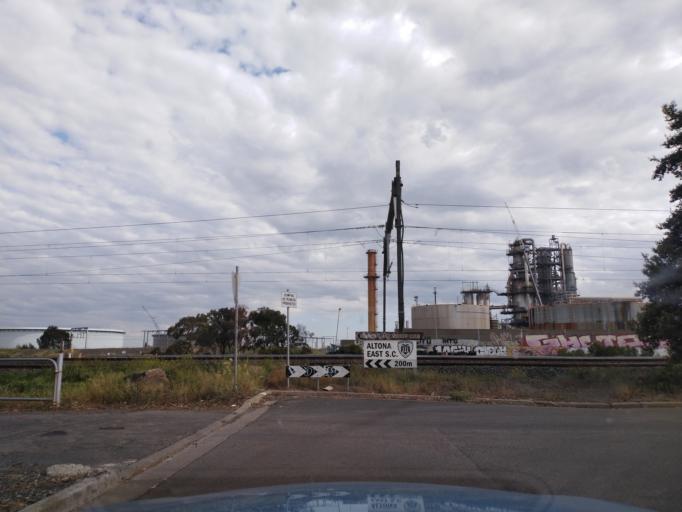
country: AU
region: Victoria
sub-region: Hobsons Bay
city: Altona North
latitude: -37.8471
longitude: 144.8538
